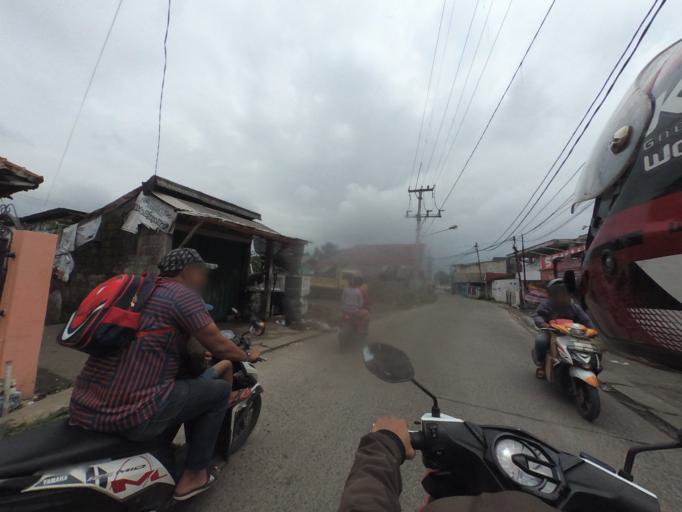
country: ID
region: West Java
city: Bogor
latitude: -6.6035
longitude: 106.7588
